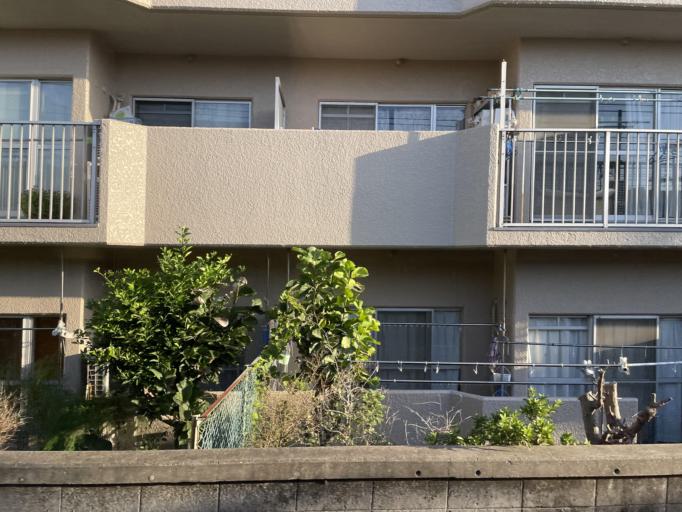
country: JP
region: Osaka
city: Matsubara
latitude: 34.5755
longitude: 135.5648
